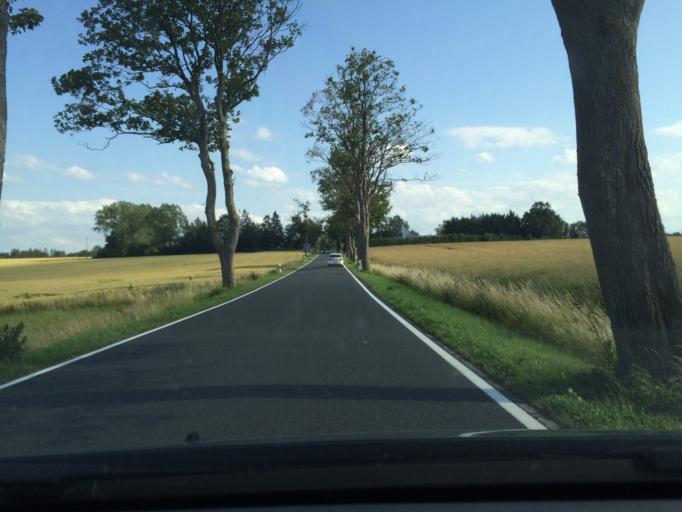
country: DE
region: Mecklenburg-Vorpommern
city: Niepars
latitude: 54.3288
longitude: 12.9352
